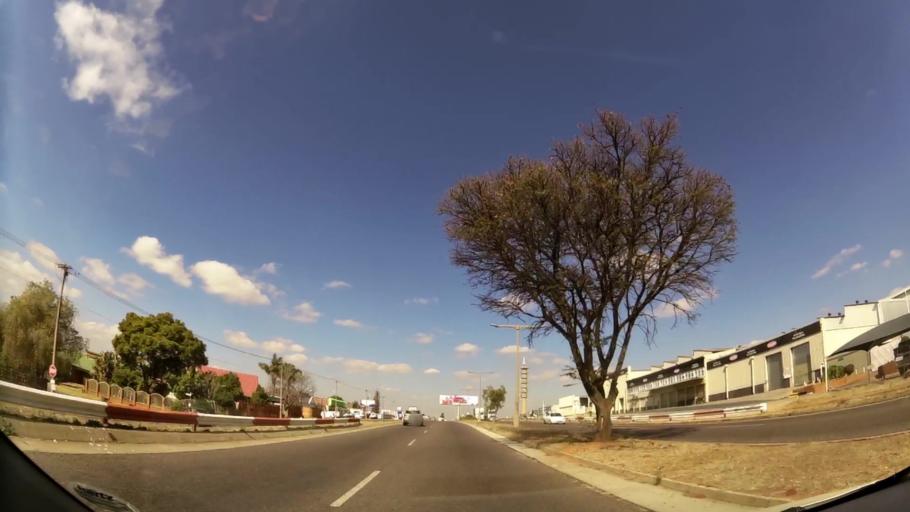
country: ZA
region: Gauteng
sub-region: West Rand District Municipality
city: Krugersdorp
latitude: -26.1171
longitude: 27.8171
